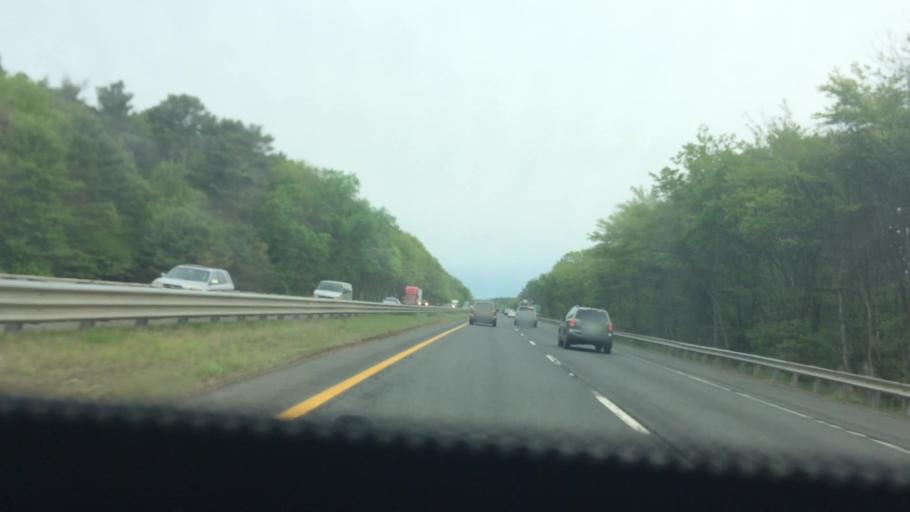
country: US
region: Massachusetts
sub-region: Worcester County
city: Fiskdale
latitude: 42.1389
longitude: -72.1327
